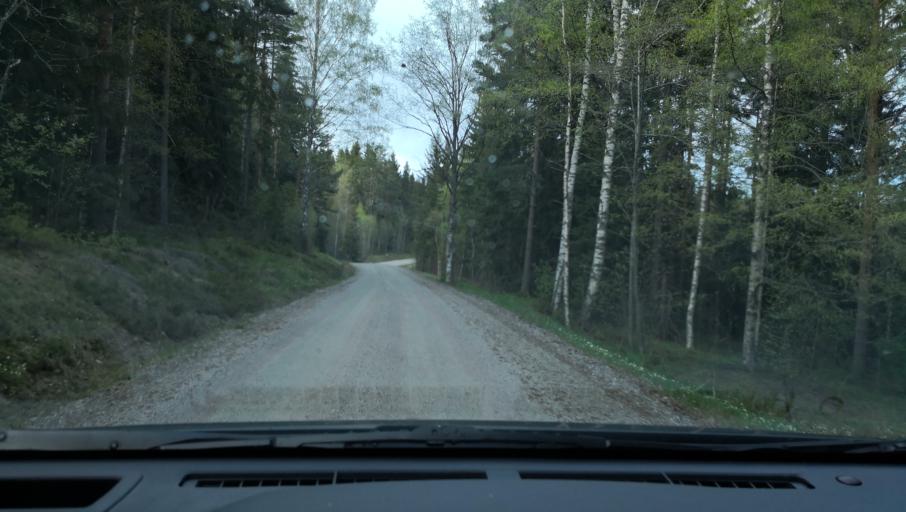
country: SE
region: Dalarna
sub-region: Saters Kommun
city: Saeter
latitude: 60.1808
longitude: 15.7275
